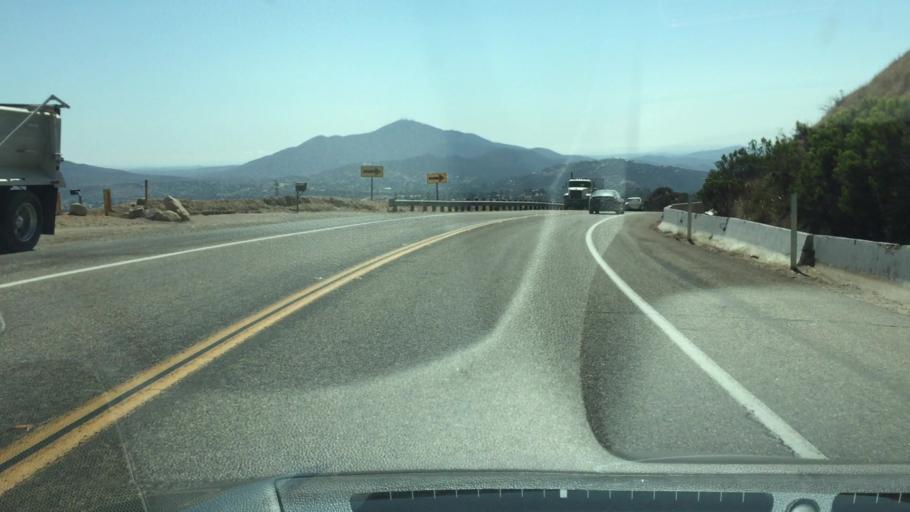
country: US
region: California
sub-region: San Diego County
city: Jamul
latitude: 32.7346
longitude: -116.8328
